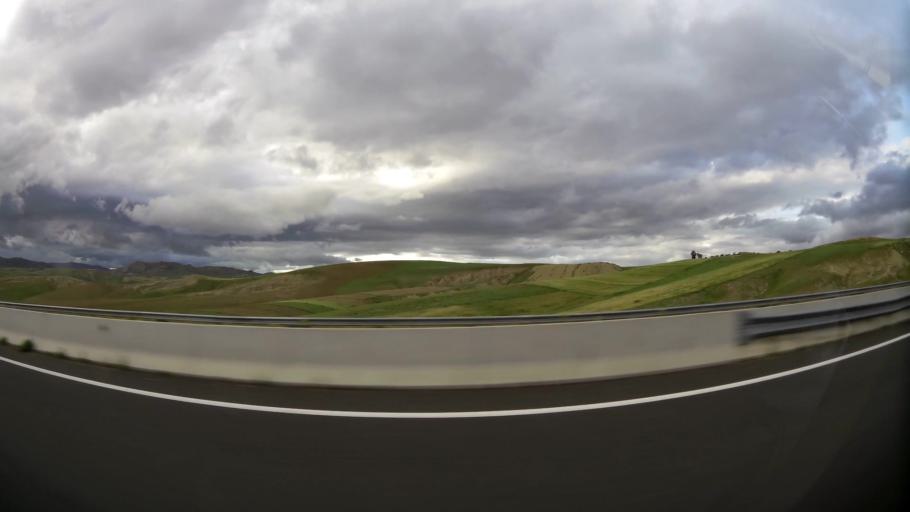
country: MA
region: Taza-Al Hoceima-Taounate
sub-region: Taza
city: Taza
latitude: 34.2513
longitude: -3.9082
